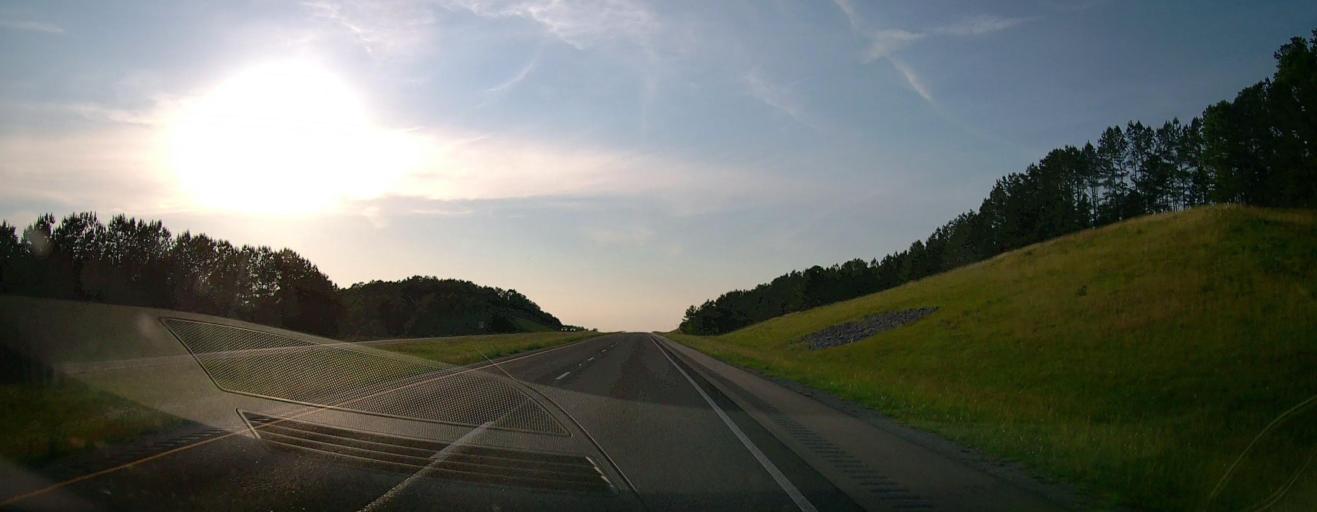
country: US
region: Alabama
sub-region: Marion County
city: Guin
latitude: 34.0534
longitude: -87.9397
